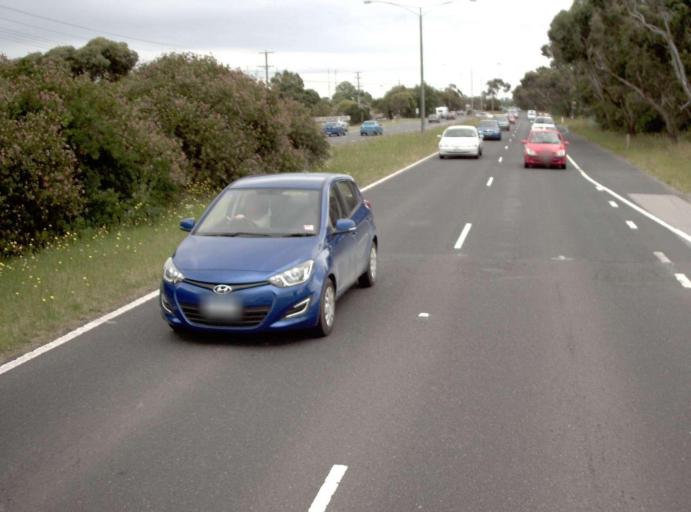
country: AU
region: Victoria
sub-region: Casey
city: Cranbourne
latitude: -38.0944
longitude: 145.2820
